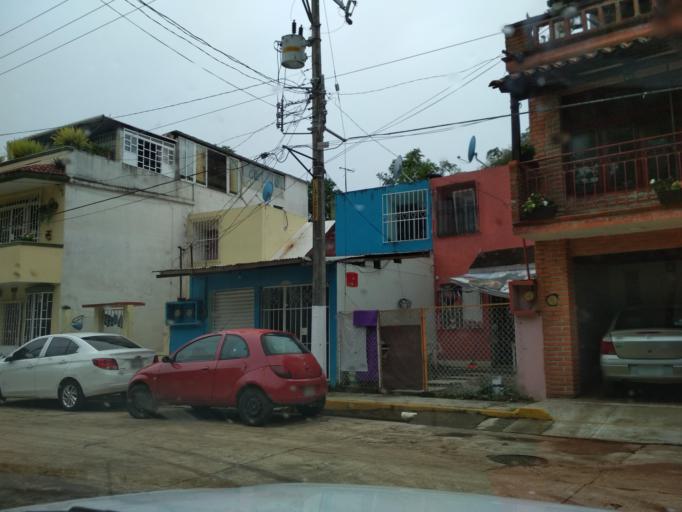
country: MX
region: Veracruz
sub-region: San Andres Tuxtla
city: Los Pinos
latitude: 18.4485
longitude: -95.2293
